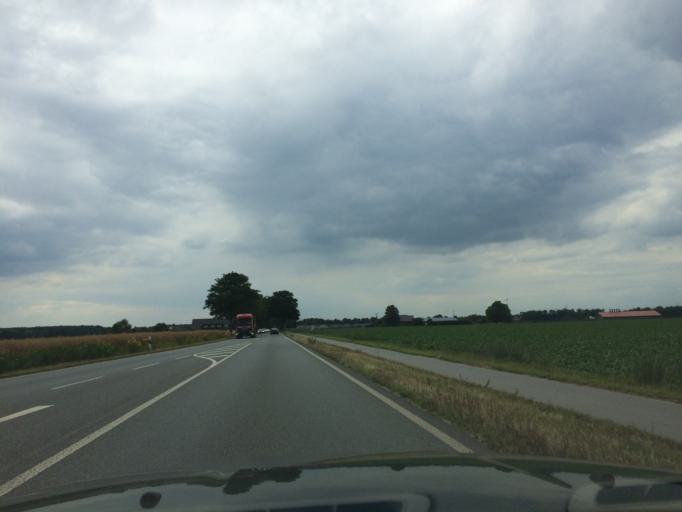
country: DE
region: North Rhine-Westphalia
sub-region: Regierungsbezirk Dusseldorf
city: Weeze
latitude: 51.6453
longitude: 6.1880
